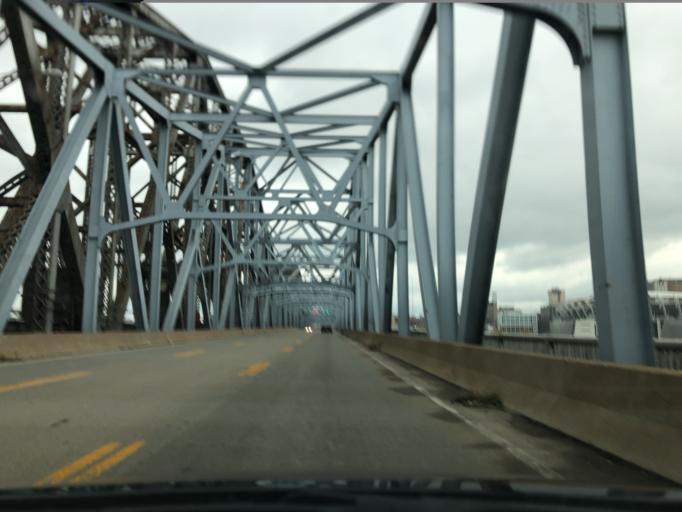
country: US
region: Kentucky
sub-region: Kenton County
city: Covington
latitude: 39.0897
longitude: -84.5189
